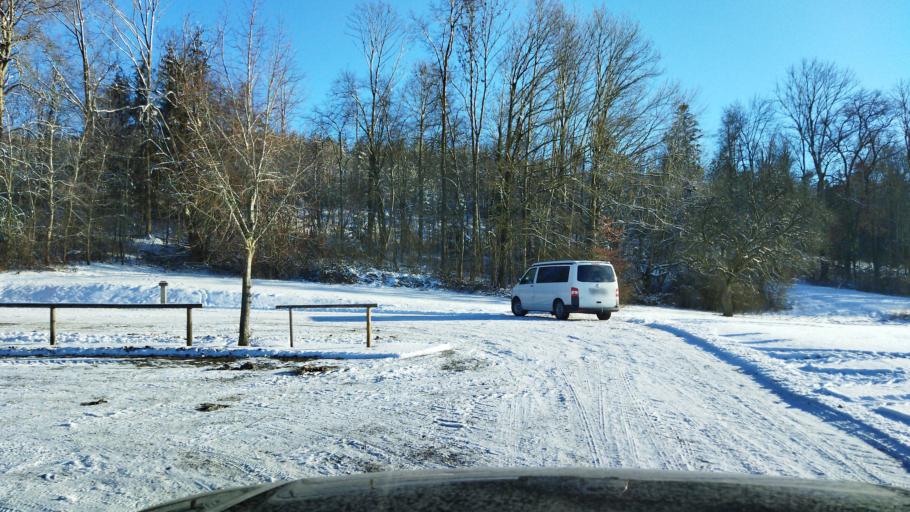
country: DE
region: Baden-Wuerttemberg
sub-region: Regierungsbezirk Stuttgart
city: Gerabronn
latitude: 48.9649
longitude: 9.8988
